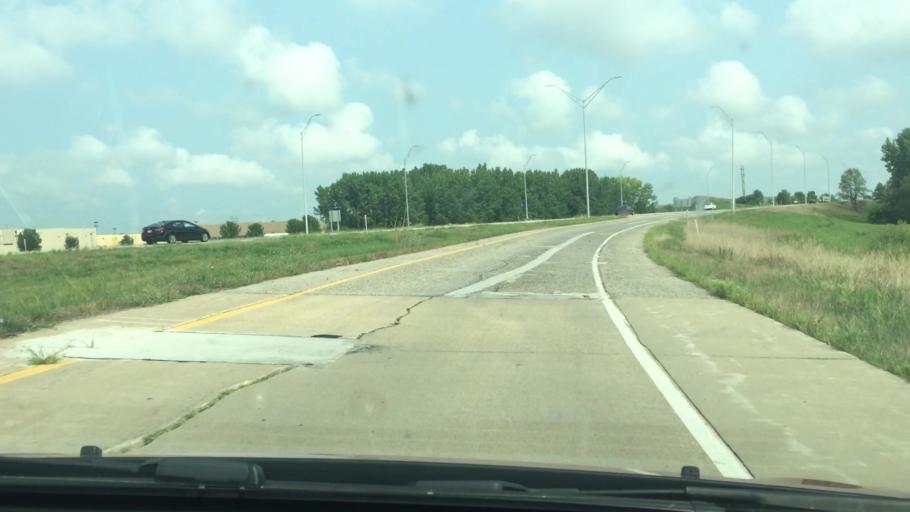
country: US
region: Iowa
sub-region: Scott County
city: Bettendorf
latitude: 41.5775
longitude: -90.5215
